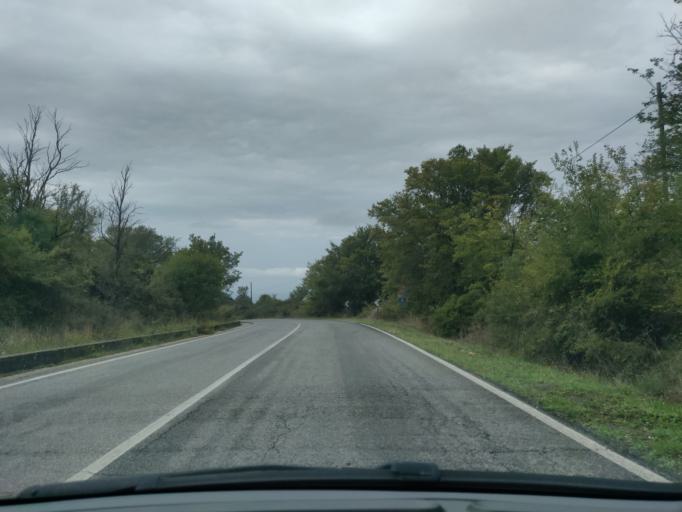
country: IT
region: Latium
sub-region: Citta metropolitana di Roma Capitale
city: Allumiere
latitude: 42.1150
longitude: 11.8585
